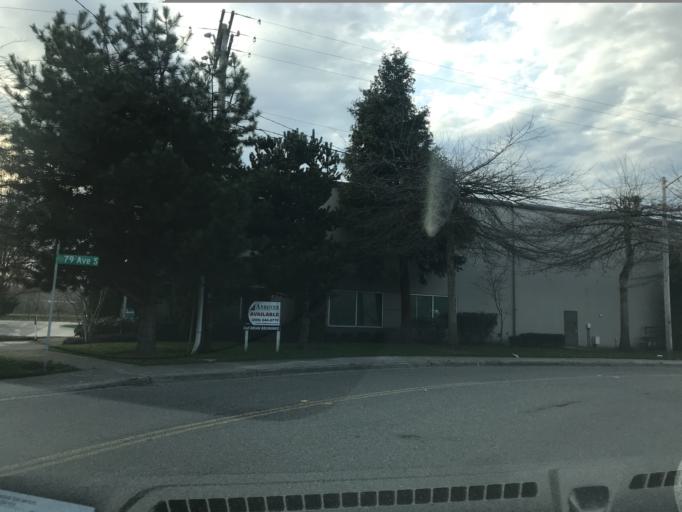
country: US
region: Washington
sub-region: King County
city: Kent
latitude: 47.3633
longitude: -122.2348
